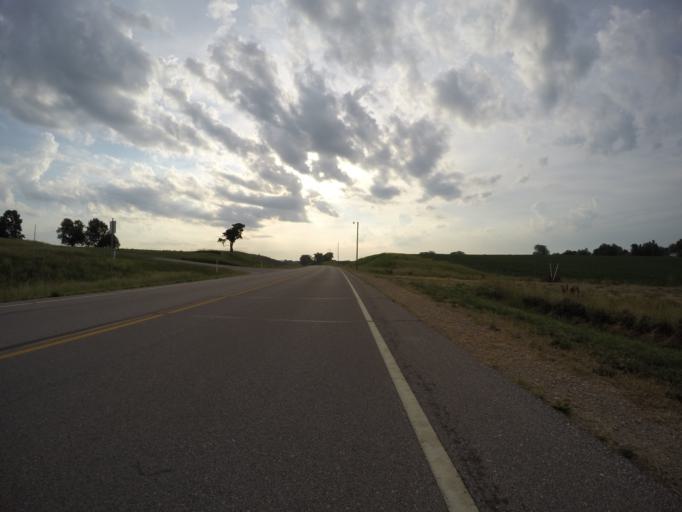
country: US
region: Kansas
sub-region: Doniphan County
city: Troy
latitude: 39.7899
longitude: -95.0832
